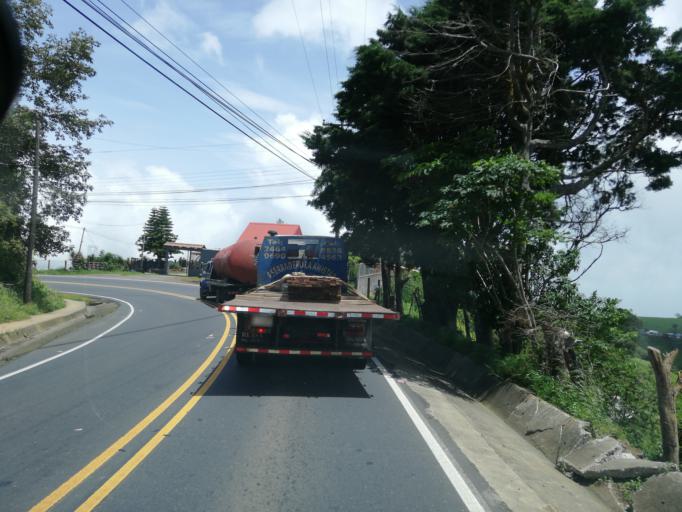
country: CR
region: Alajuela
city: Zarcero
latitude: 10.2222
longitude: -84.4062
